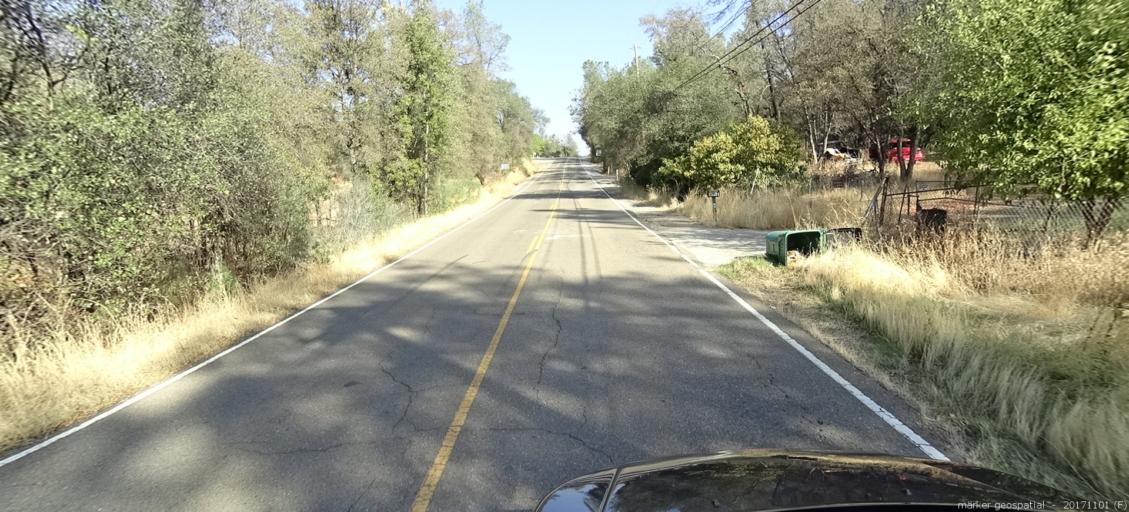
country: US
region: California
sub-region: Shasta County
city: Shasta Lake
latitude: 40.6801
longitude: -122.3184
